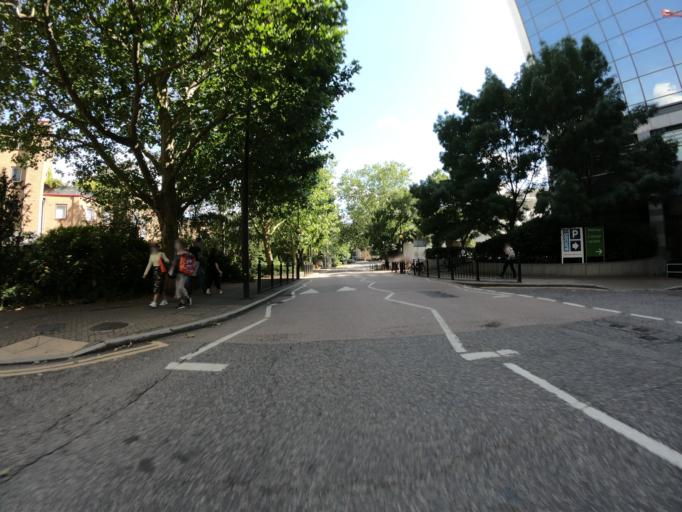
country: GB
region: England
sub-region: Greater London
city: Bethnal Green
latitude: 51.5075
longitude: -0.0667
